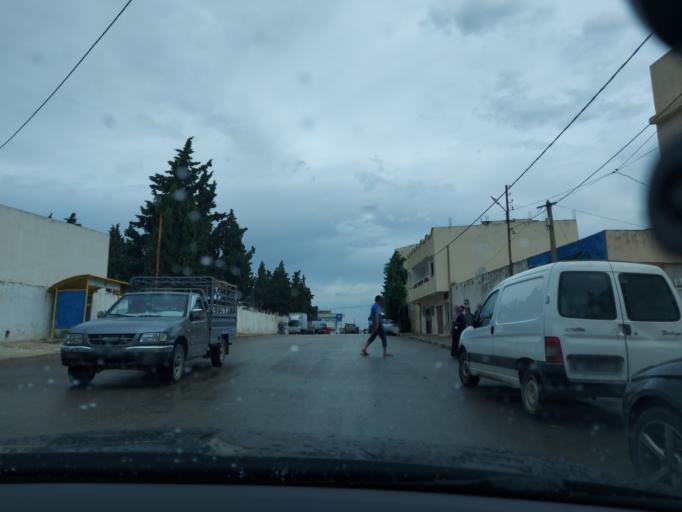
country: TN
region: Silyanah
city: Maktar
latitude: 35.8556
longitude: 9.2033
